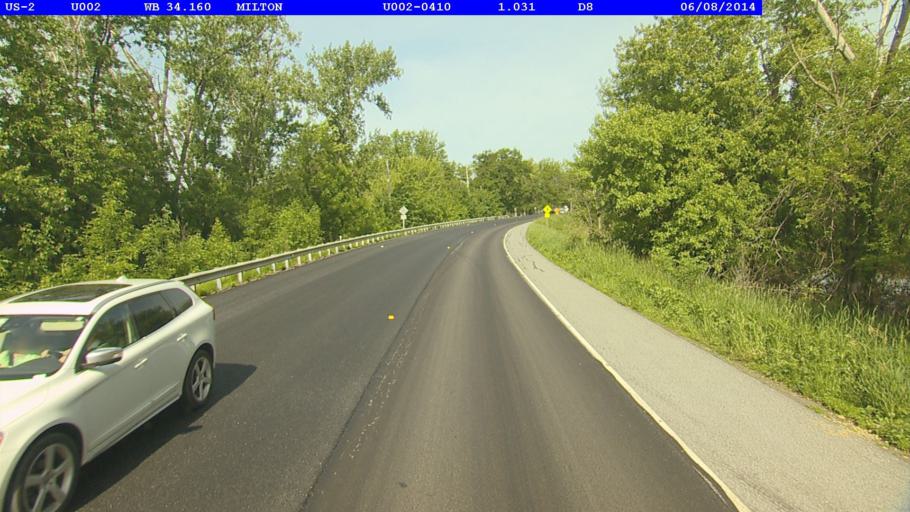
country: US
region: Vermont
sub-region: Chittenden County
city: Colchester
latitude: 44.6253
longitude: -73.2371
